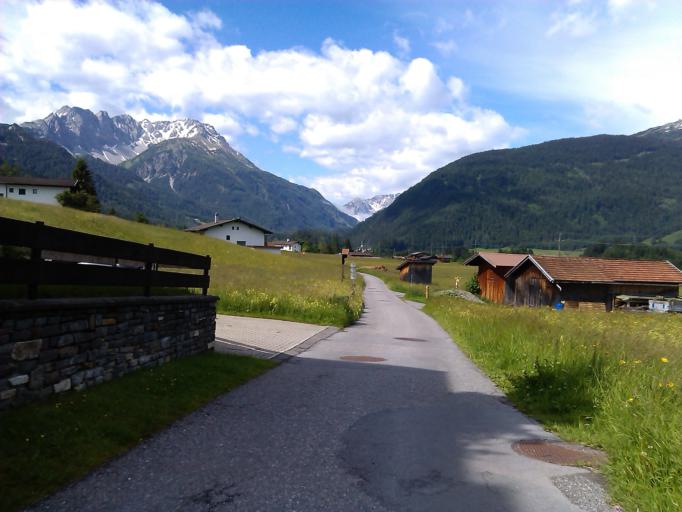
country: AT
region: Tyrol
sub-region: Politischer Bezirk Reutte
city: Ehrwald
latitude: 47.3990
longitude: 10.9165
